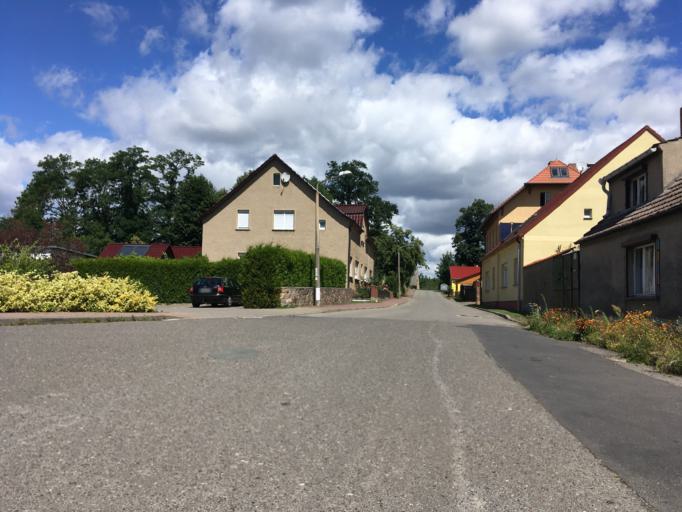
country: DE
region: Brandenburg
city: Gerswalde
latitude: 53.1720
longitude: 13.7528
